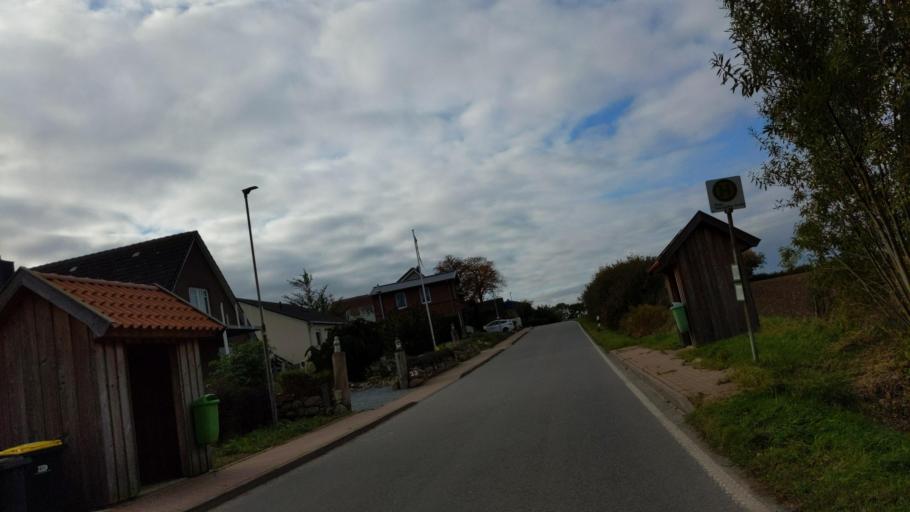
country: DE
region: Schleswig-Holstein
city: Sierksdorf
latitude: 54.1017
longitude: 10.7733
